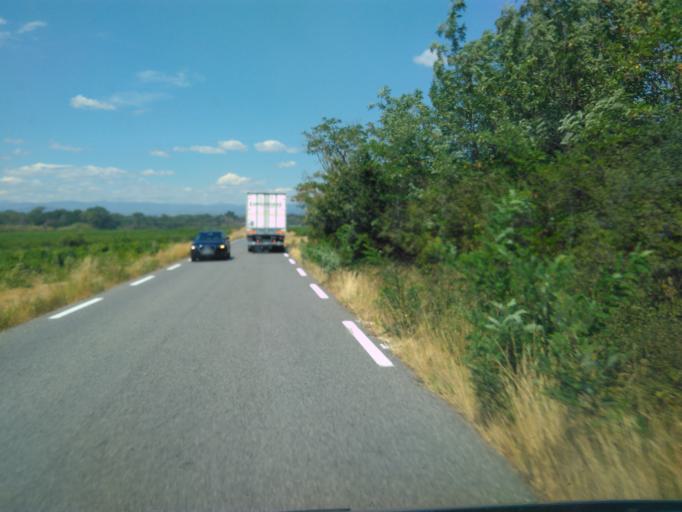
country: FR
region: Provence-Alpes-Cote d'Azur
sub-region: Departement du Var
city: La Garde-Freinet
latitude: 43.3380
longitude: 6.4273
